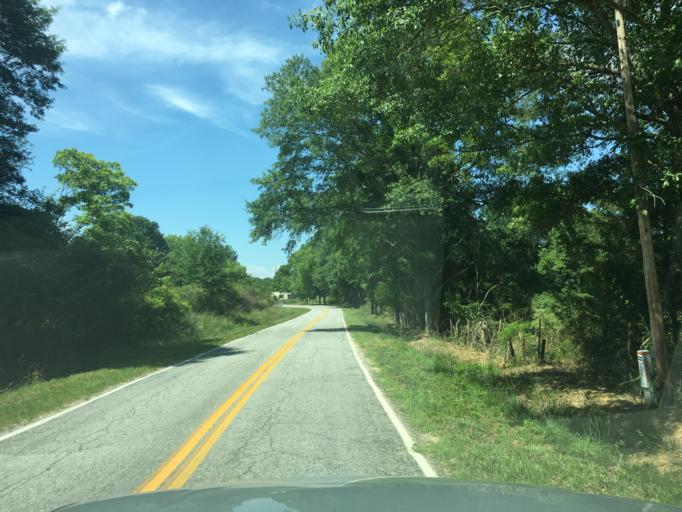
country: US
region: Georgia
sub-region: Hart County
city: Reed Creek
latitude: 34.5078
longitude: -82.9818
